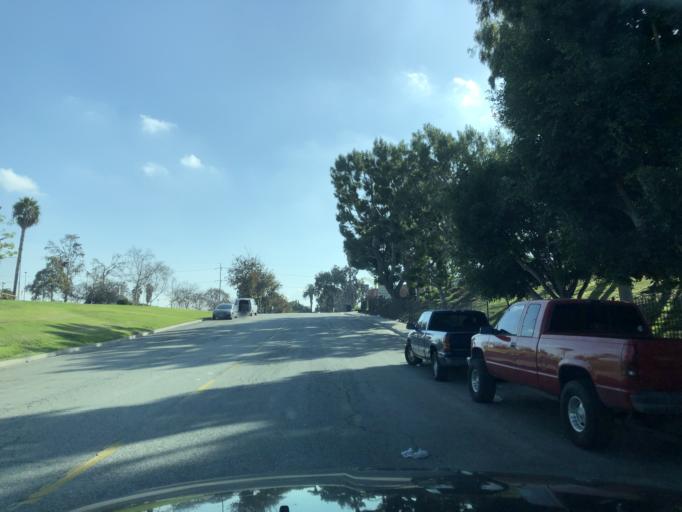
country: US
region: California
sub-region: Los Angeles County
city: Inglewood
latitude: 33.9678
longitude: -118.3614
